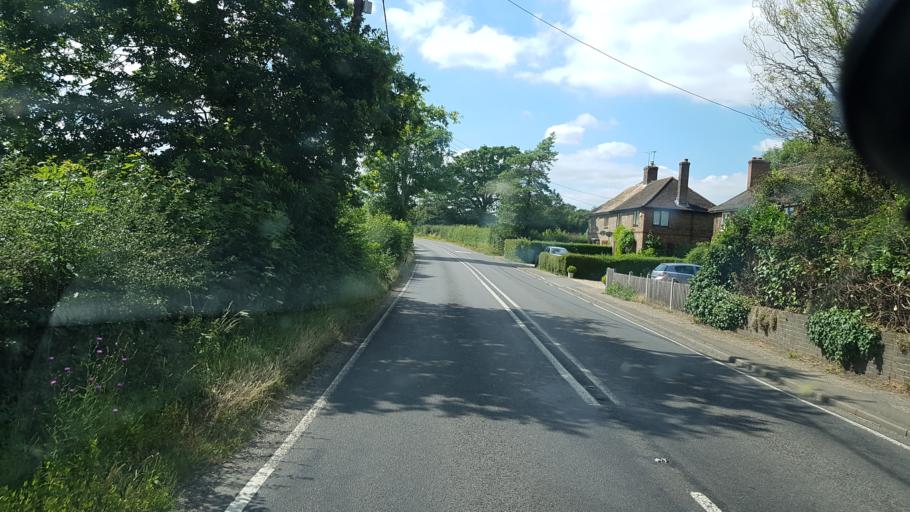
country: GB
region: England
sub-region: West Sussex
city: Partridge Green
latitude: 50.9910
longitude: -0.2764
